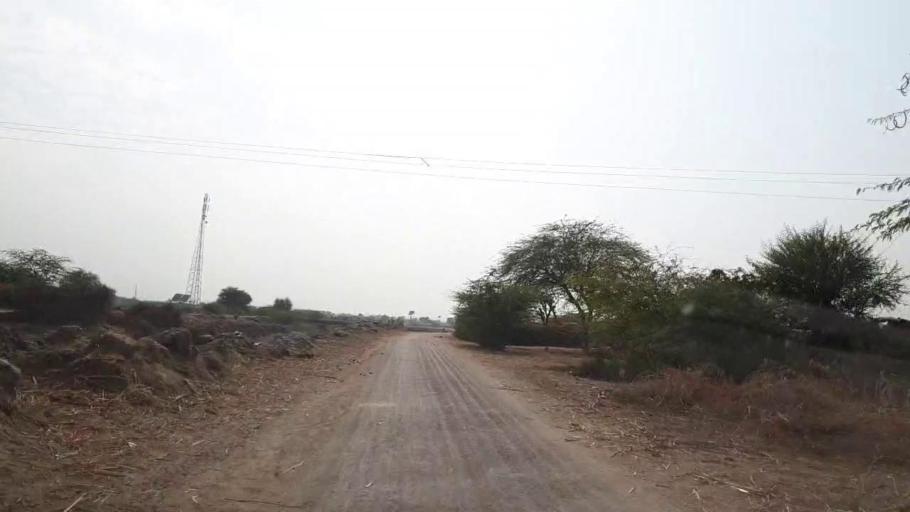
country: PK
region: Sindh
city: Mirpur Khas
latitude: 25.5426
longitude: 69.1619
